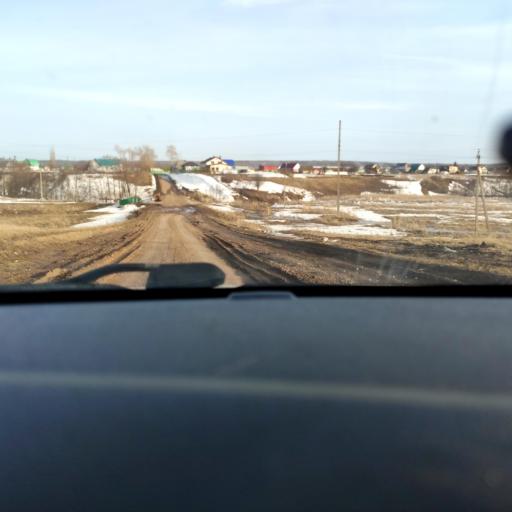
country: RU
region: Bashkortostan
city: Avdon
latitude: 54.4862
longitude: 55.5921
